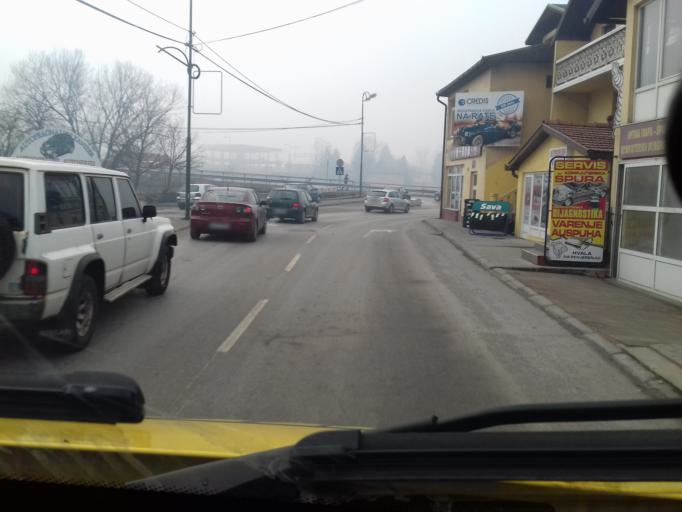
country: BA
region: Federation of Bosnia and Herzegovina
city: Kakanj
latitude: 44.1244
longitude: 18.1133
